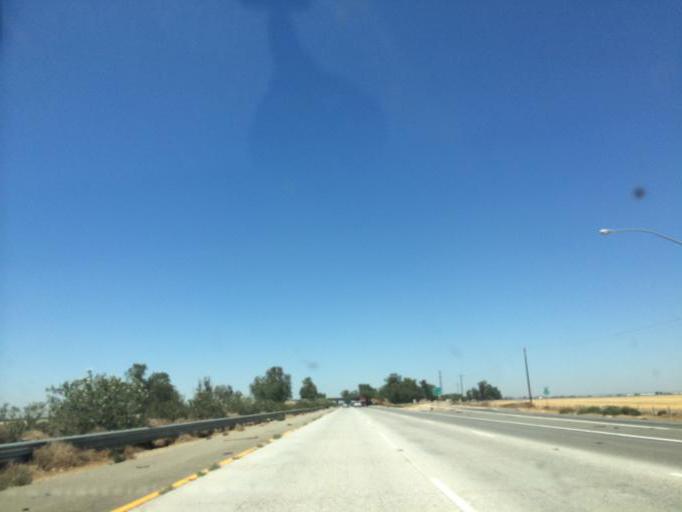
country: US
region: California
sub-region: Kern County
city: Greenfield
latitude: 35.1681
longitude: -119.0028
